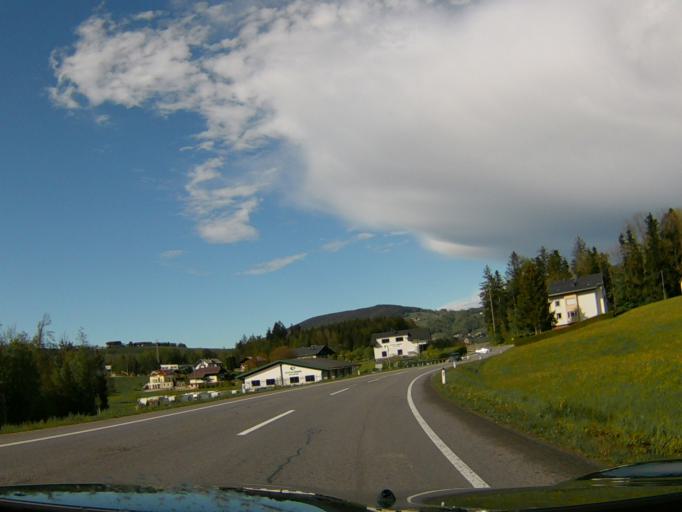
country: AT
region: Upper Austria
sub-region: Politischer Bezirk Vocklabruck
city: Mondsee
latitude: 47.8429
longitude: 13.3186
